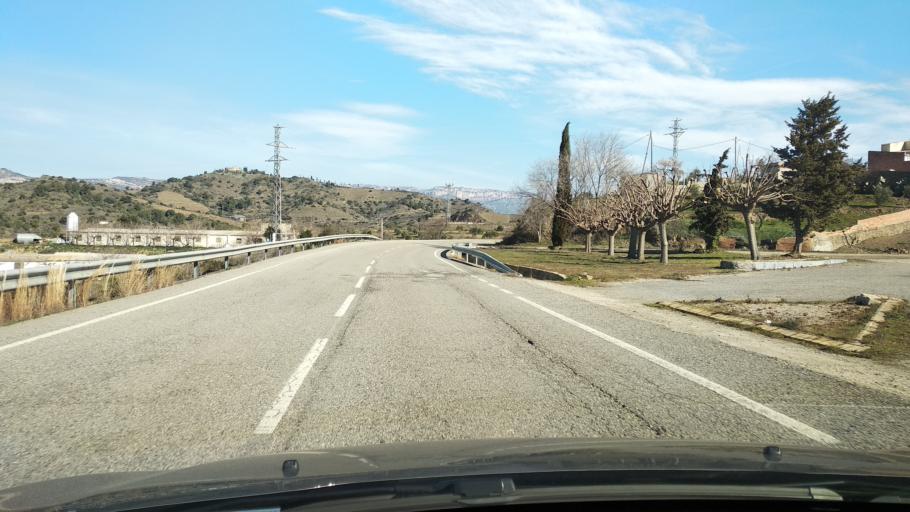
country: ES
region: Catalonia
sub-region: Provincia de Tarragona
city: Falset
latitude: 41.1943
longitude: 0.7766
